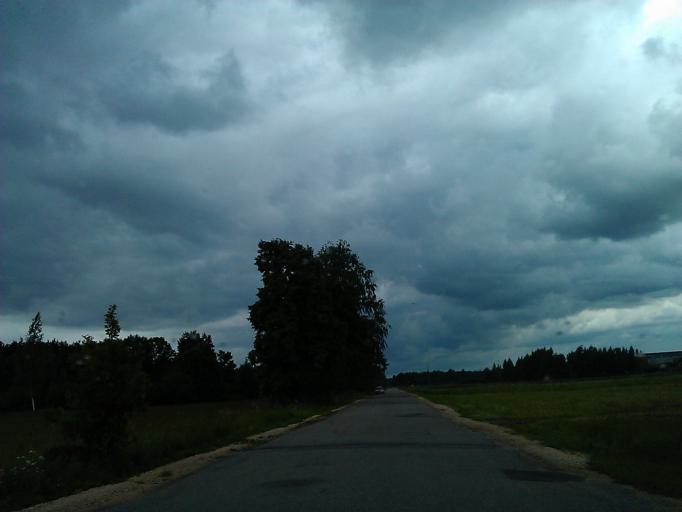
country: LV
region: Adazi
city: Adazi
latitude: 57.0832
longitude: 24.2948
